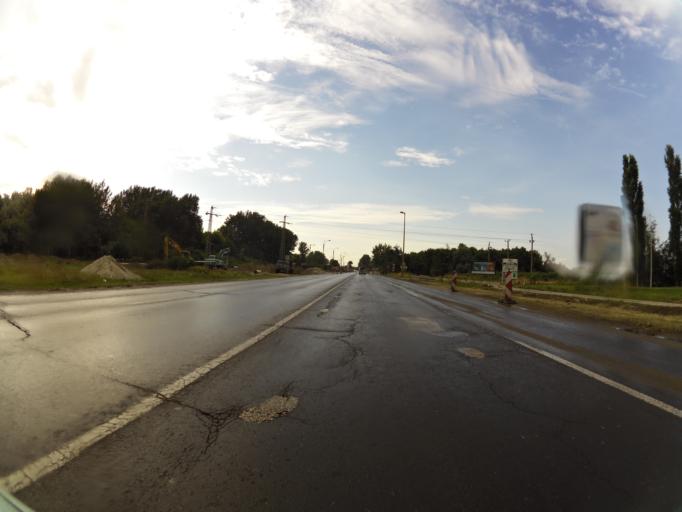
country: HU
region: Csongrad
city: Szeged
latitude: 46.2740
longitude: 20.1007
